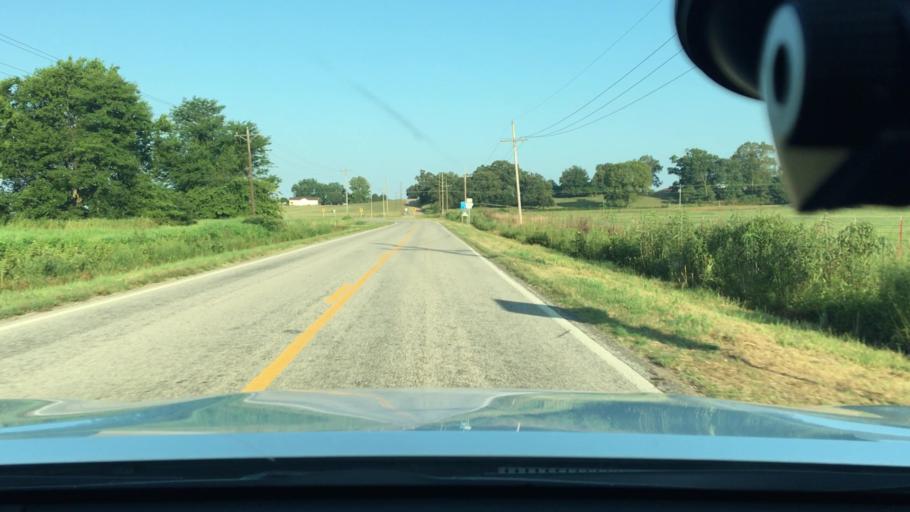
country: US
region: Arkansas
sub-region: Johnson County
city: Coal Hill
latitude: 35.3377
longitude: -93.6283
